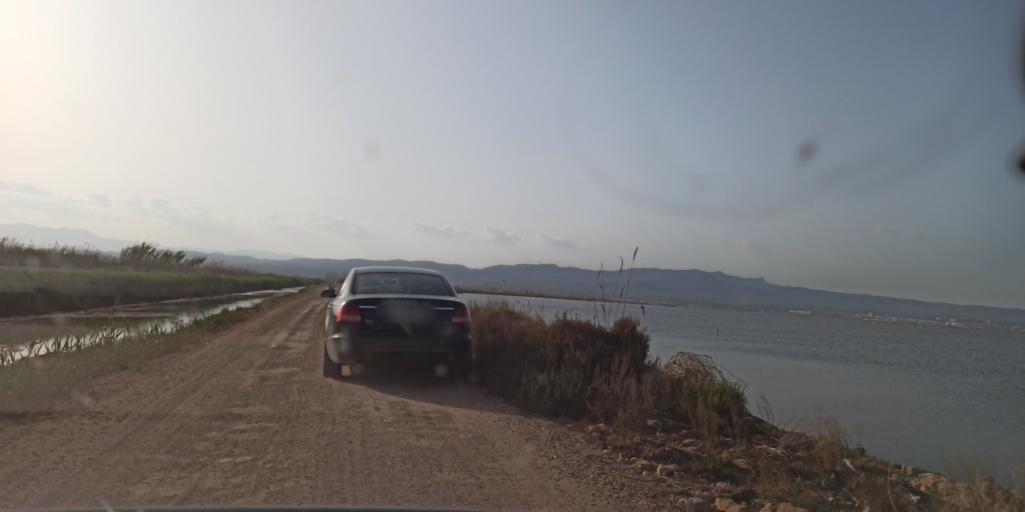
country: ES
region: Catalonia
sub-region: Provincia de Tarragona
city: L'Ampolla
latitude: 40.7682
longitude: 0.7334
